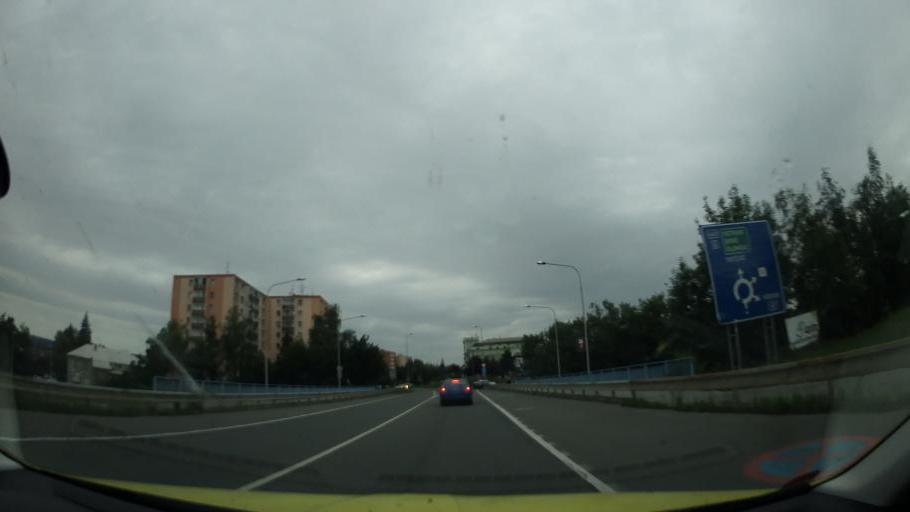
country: CZ
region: Olomoucky
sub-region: Okres Prerov
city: Hranice
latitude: 49.5559
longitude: 17.7352
